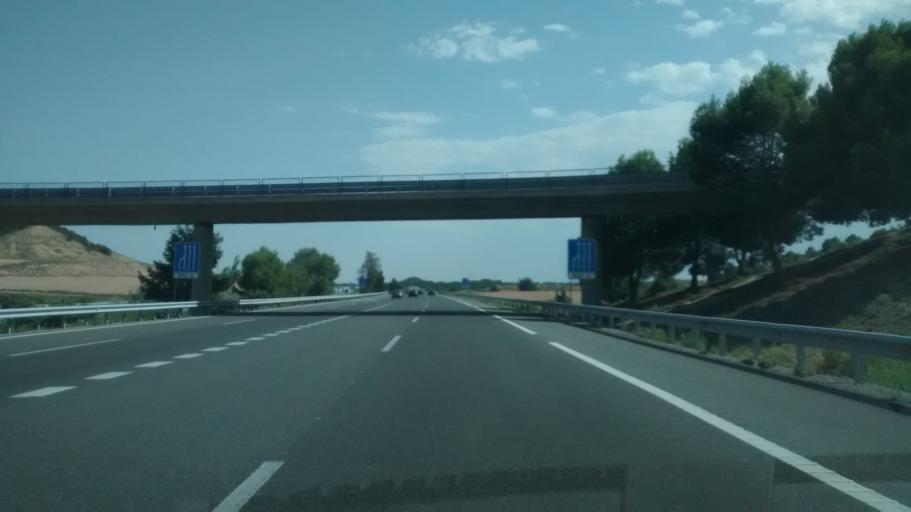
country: ES
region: Navarre
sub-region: Provincia de Navarra
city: Corella
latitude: 42.0920
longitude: -1.7198
